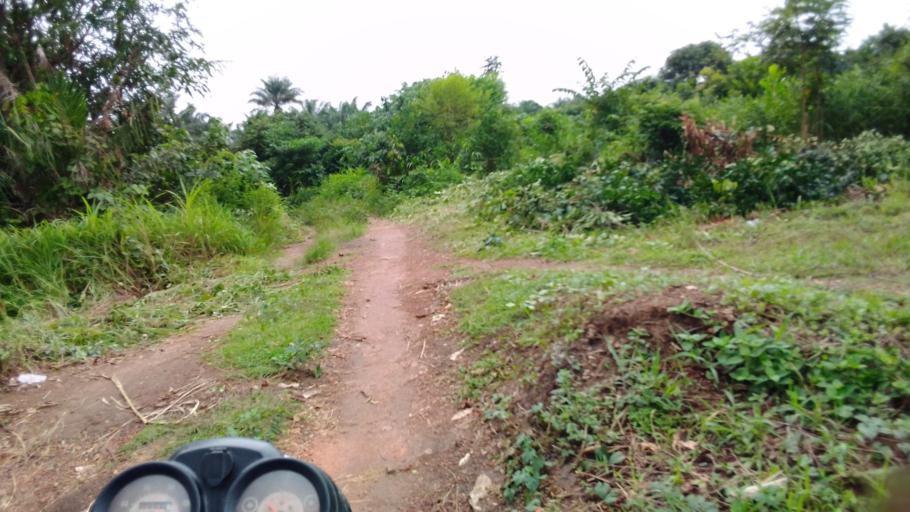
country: SL
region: Eastern Province
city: Kenema
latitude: 7.8678
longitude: -11.1675
